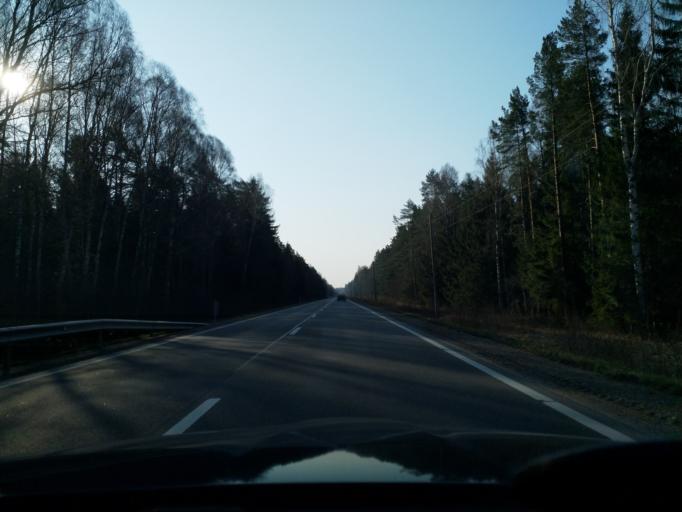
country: LV
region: Rucavas
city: Rucava
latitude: 56.2267
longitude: 21.1155
